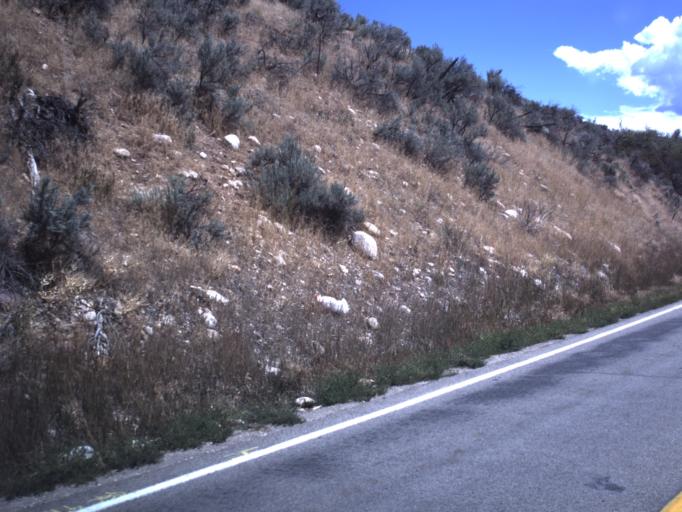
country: US
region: Utah
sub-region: Summit County
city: Oakley
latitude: 40.7235
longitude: -111.3229
